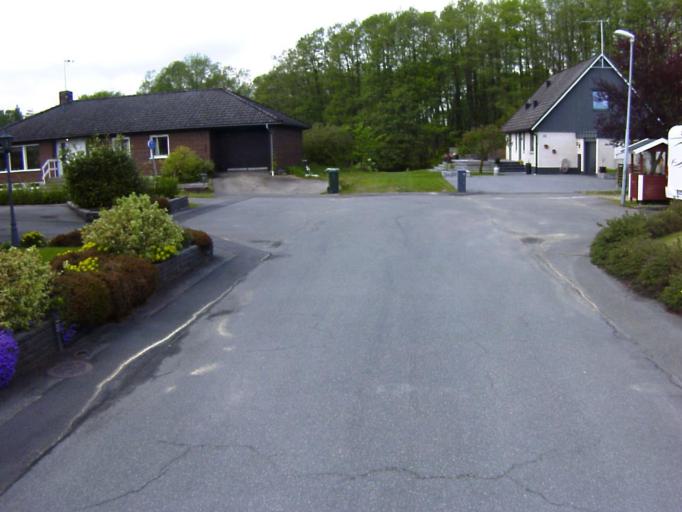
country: SE
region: Skane
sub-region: Kristianstads Kommun
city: Degeberga
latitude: 55.8259
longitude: 14.0917
